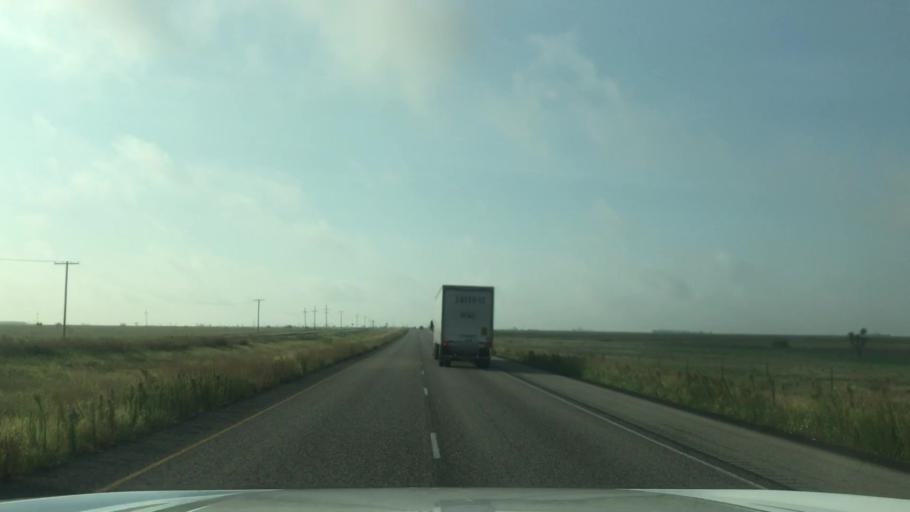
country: US
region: Texas
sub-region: Garza County
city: Post
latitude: 33.2509
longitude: -101.4657
